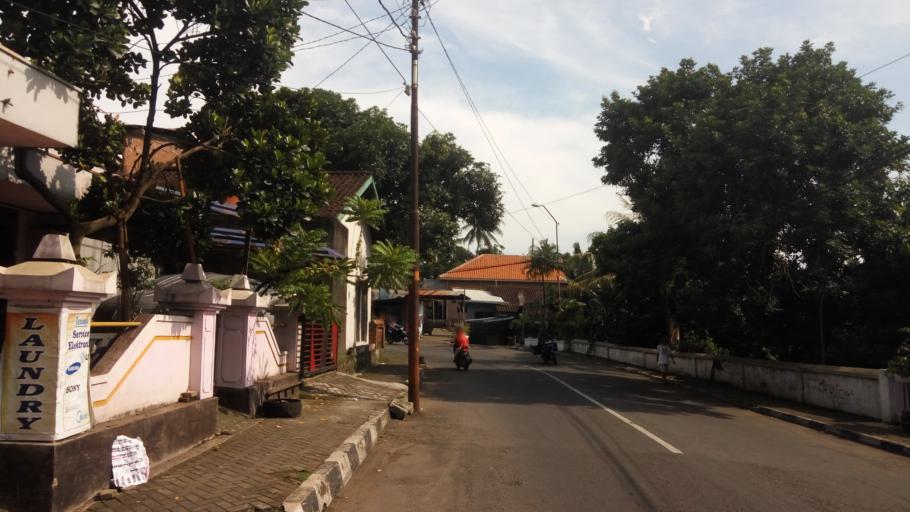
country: ID
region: Central Java
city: Ungaran
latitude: -7.1375
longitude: 110.4102
